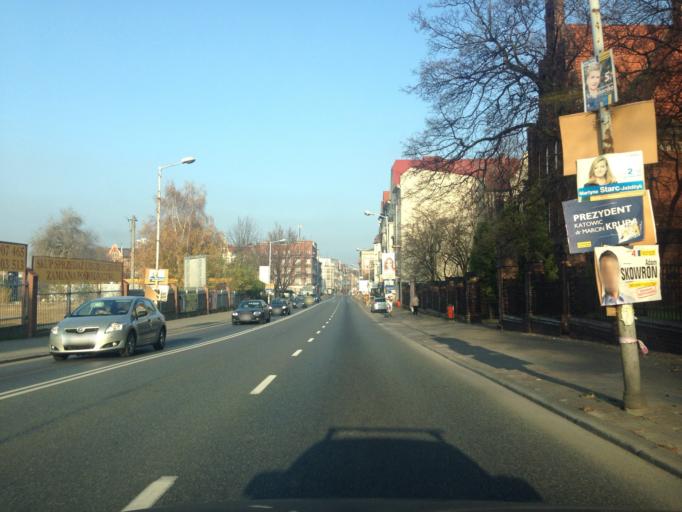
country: PL
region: Silesian Voivodeship
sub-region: Katowice
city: Katowice
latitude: 50.2534
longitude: 19.0095
